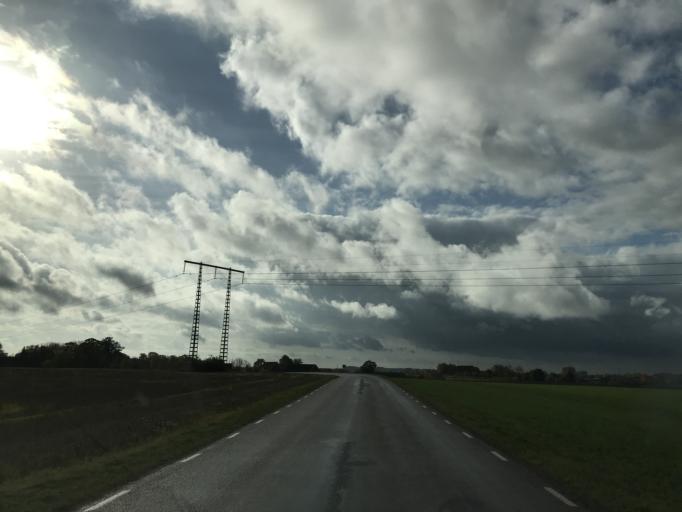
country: SE
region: Skane
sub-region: Svalovs Kommun
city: Teckomatorp
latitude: 55.8758
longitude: 13.1183
